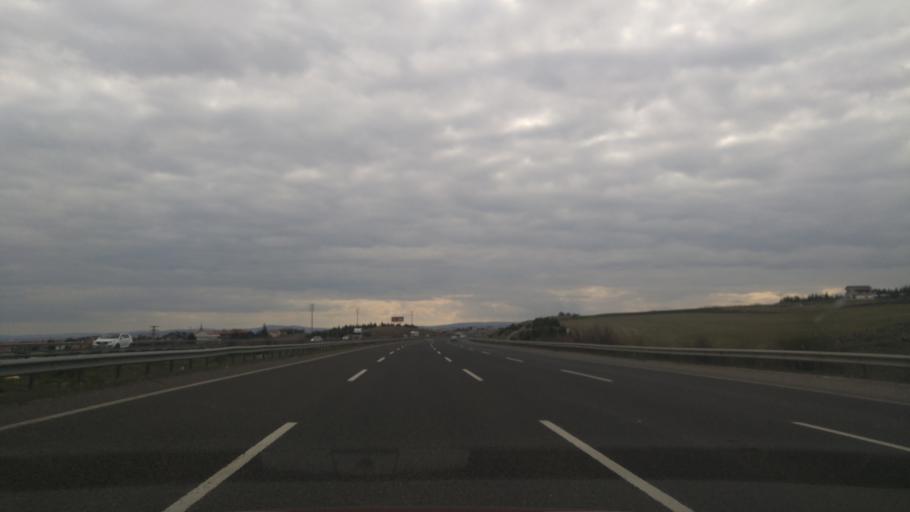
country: TR
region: Ankara
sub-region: Goelbasi
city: Golbasi
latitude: 39.7943
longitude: 32.7863
